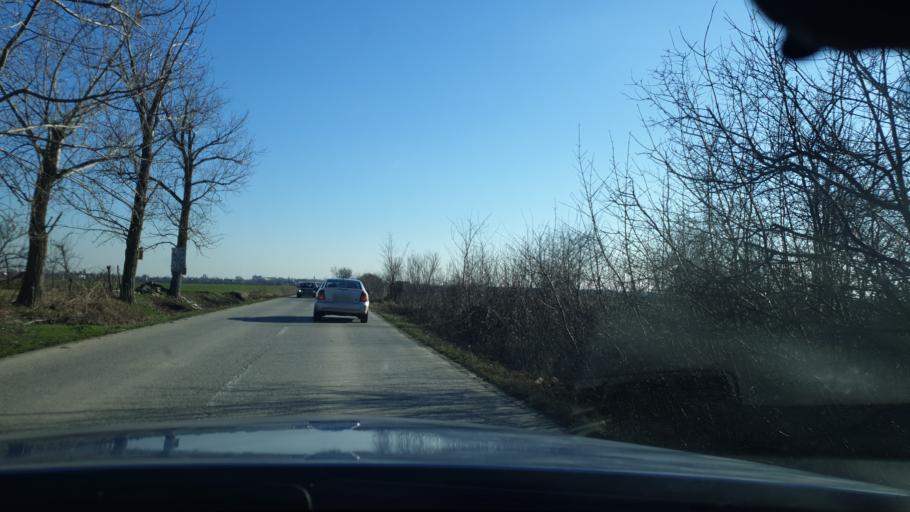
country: RS
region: Autonomna Pokrajina Vojvodina
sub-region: Sremski Okrug
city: Ruma
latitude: 45.0343
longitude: 19.8088
